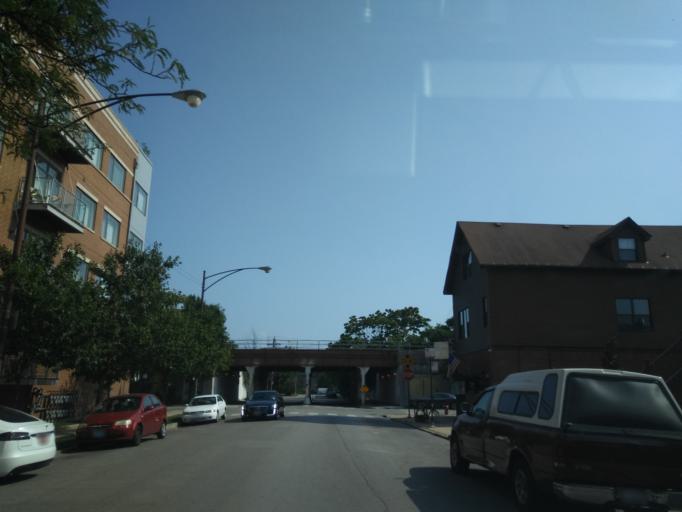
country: US
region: Illinois
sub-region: Cook County
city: Chicago
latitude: 41.8904
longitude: -87.6574
